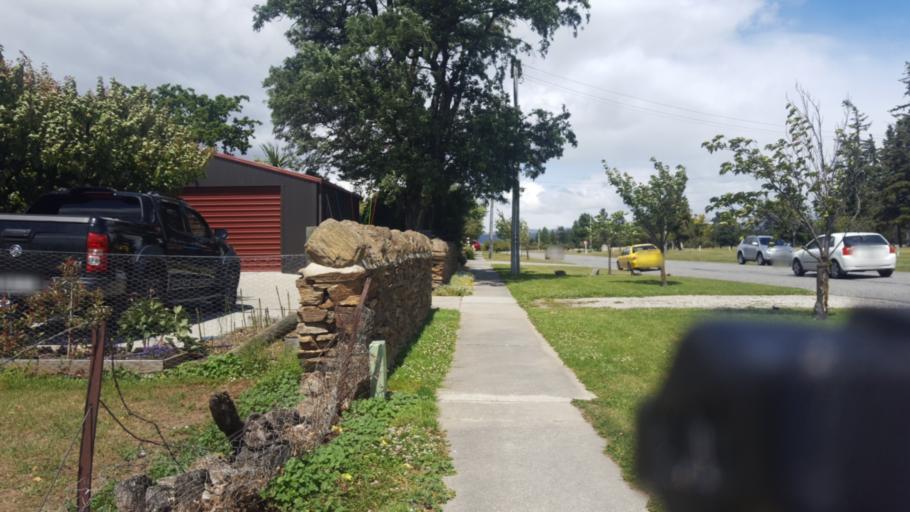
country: NZ
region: Otago
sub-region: Queenstown-Lakes District
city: Wanaka
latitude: -45.1938
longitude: 169.3258
